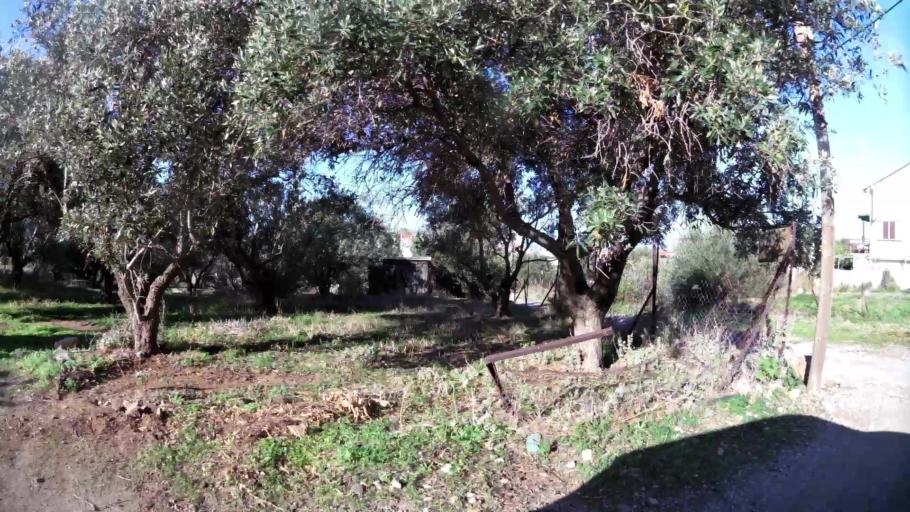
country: GR
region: Attica
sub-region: Nomarchia Athinas
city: Glyfada
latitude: 37.8708
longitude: 23.7742
